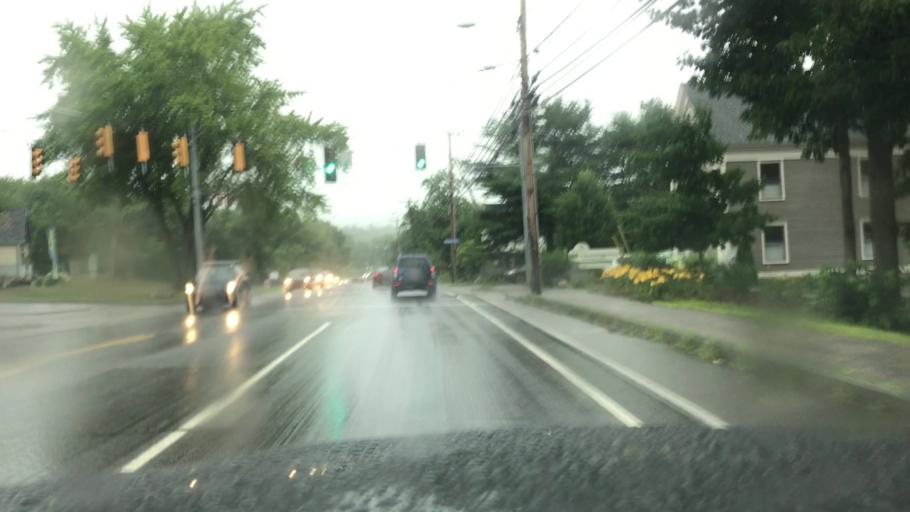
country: US
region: Maine
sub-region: York County
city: Kennebunk
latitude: 43.3993
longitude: -70.5286
